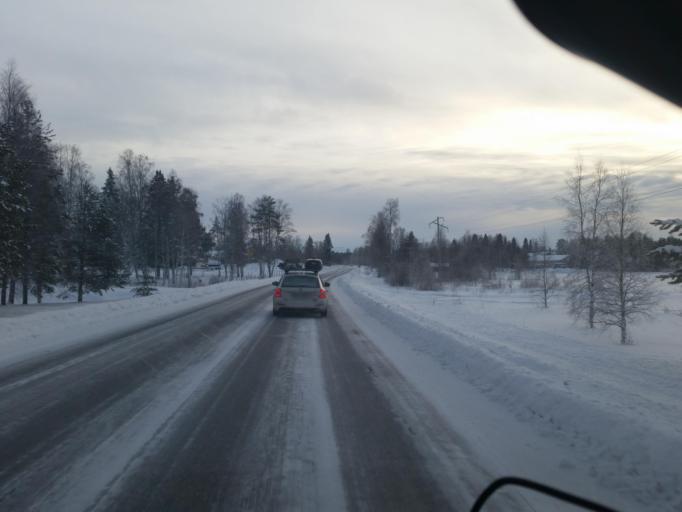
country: SE
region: Norrbotten
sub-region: Pitea Kommun
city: Norrfjarden
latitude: 65.4296
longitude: 21.4913
